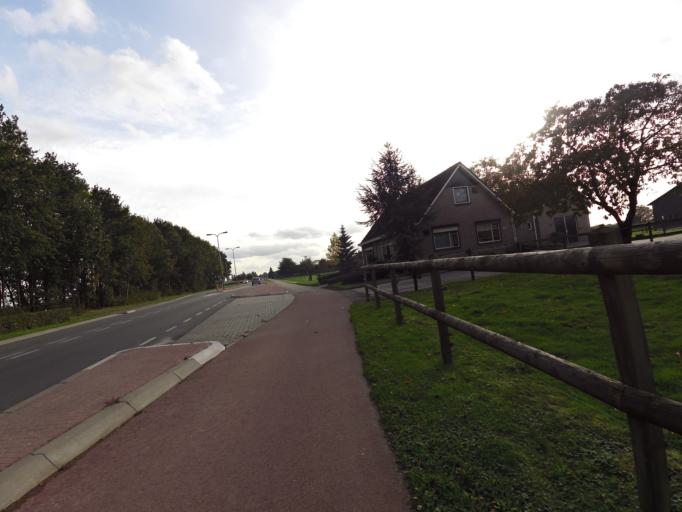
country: NL
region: Gelderland
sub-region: Gemeente Bronckhorst
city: Baak
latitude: 52.0517
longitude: 6.2214
